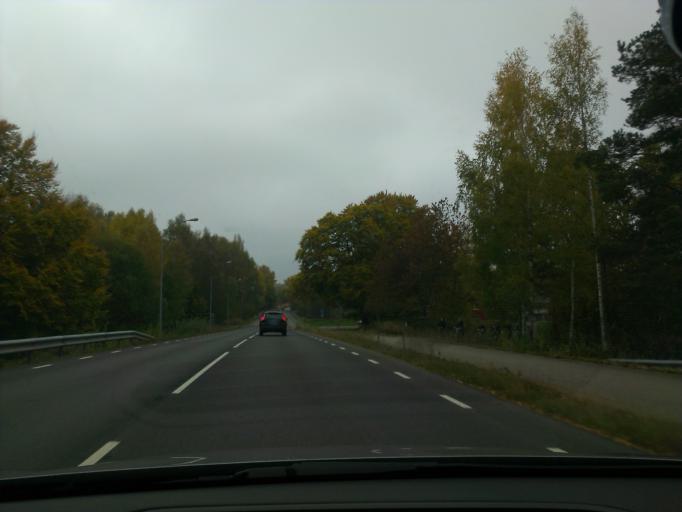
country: SE
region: Kronoberg
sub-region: Vaxjo Kommun
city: Vaexjoe
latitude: 56.8876
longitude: 14.7482
